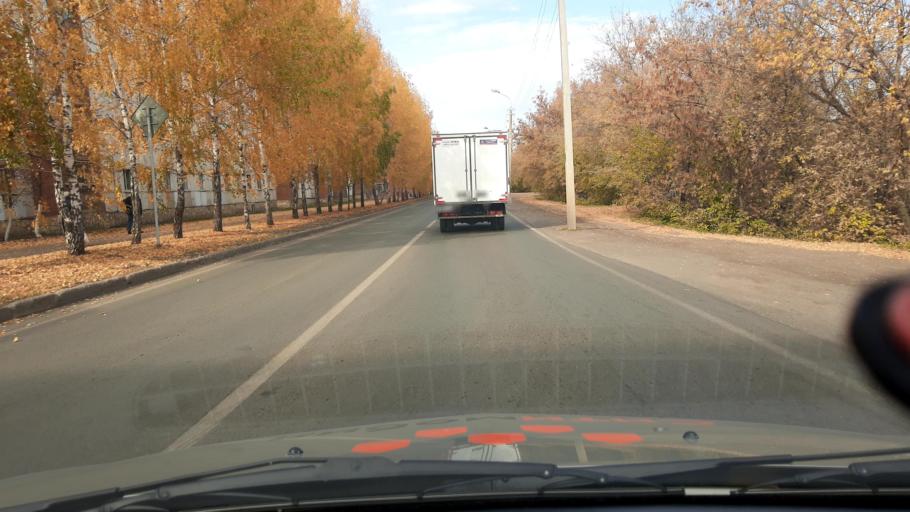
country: RU
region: Bashkortostan
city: Mikhaylovka
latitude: 54.7075
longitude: 55.8408
